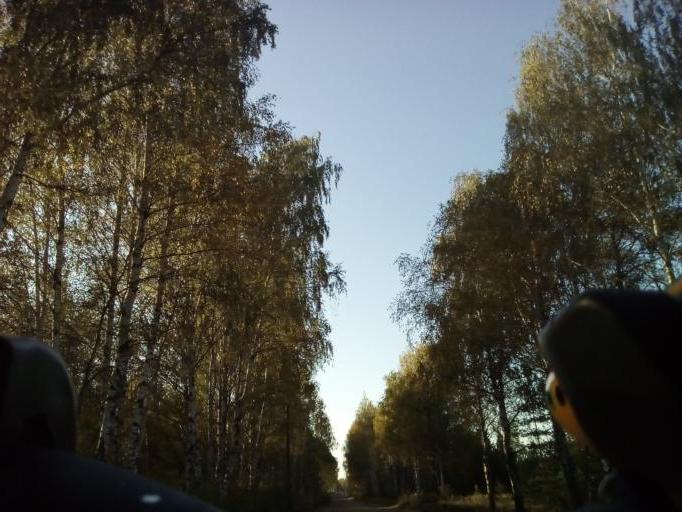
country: RU
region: Moskovskaya
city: Gzhel'
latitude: 55.6019
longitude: 38.3134
